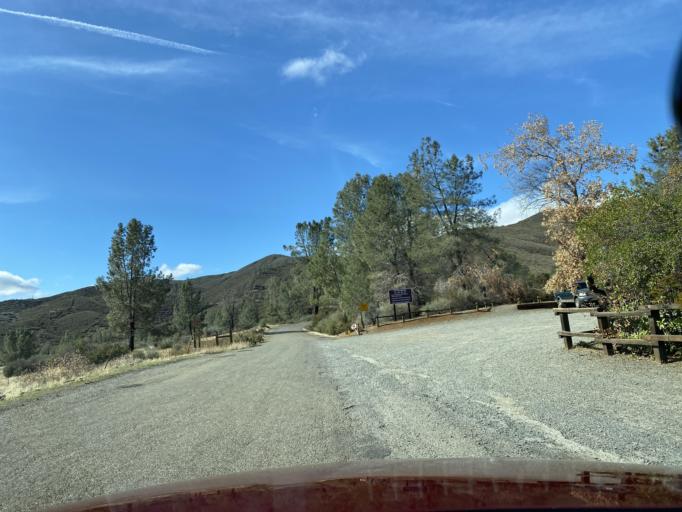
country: US
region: California
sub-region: Lake County
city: Lucerne
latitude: 39.3656
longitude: -122.6213
